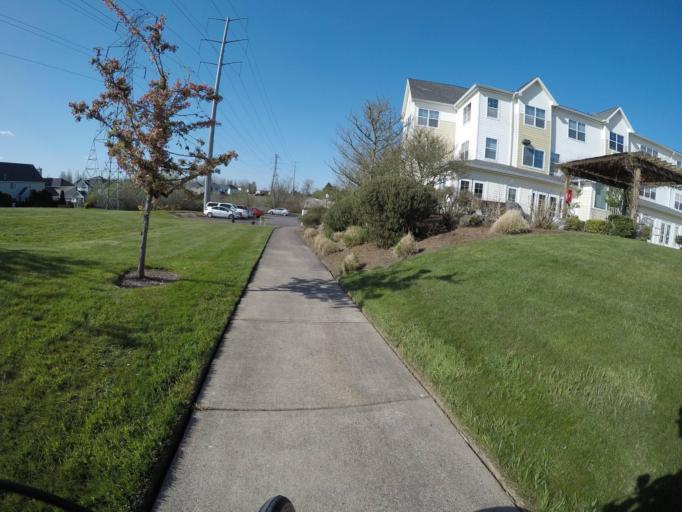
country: US
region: Oregon
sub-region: Washington County
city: Oak Hills
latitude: 45.5491
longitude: -122.8468
